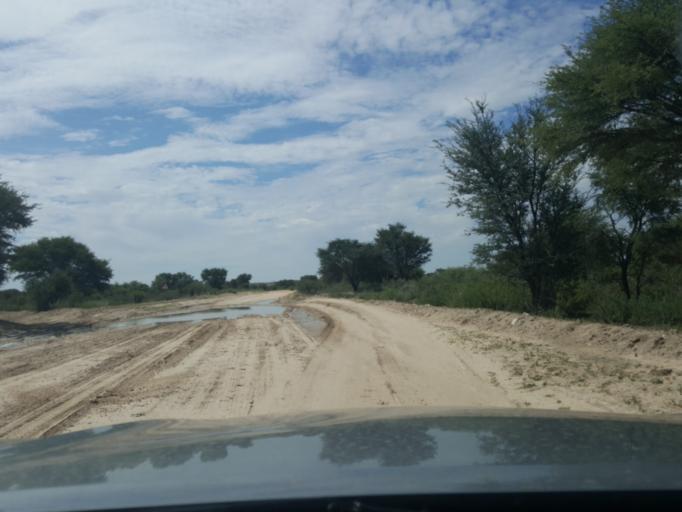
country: BW
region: Kweneng
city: Letlhakeng
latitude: -24.0649
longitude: 25.0308
